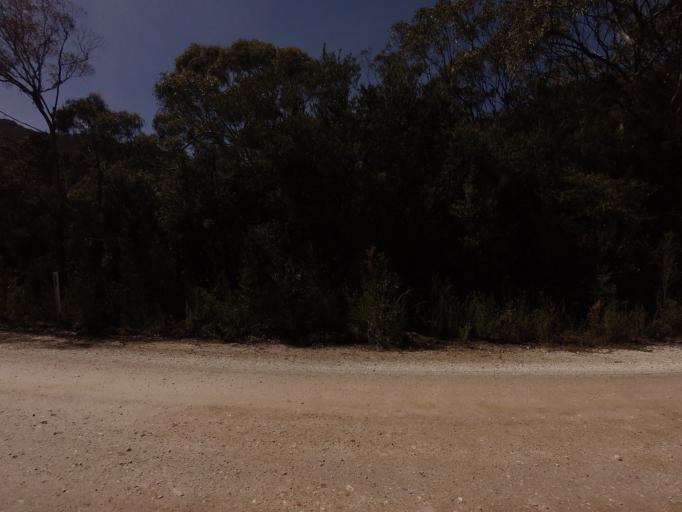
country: AU
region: Tasmania
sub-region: Huon Valley
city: Geeveston
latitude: -42.9390
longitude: 146.3482
